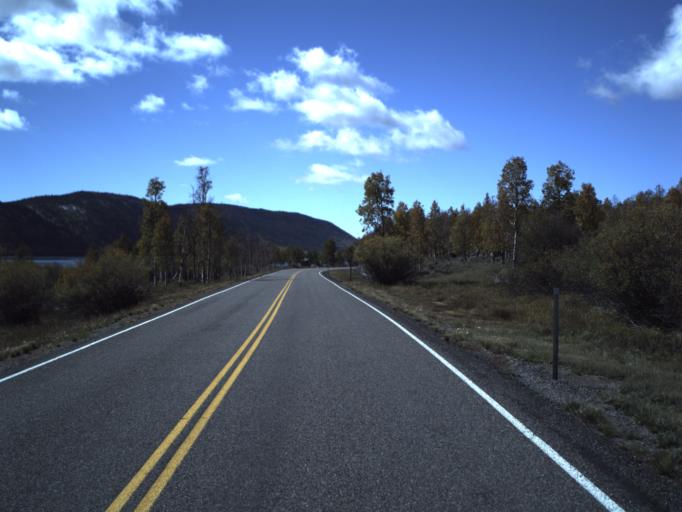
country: US
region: Utah
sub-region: Wayne County
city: Loa
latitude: 38.5611
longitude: -111.7079
